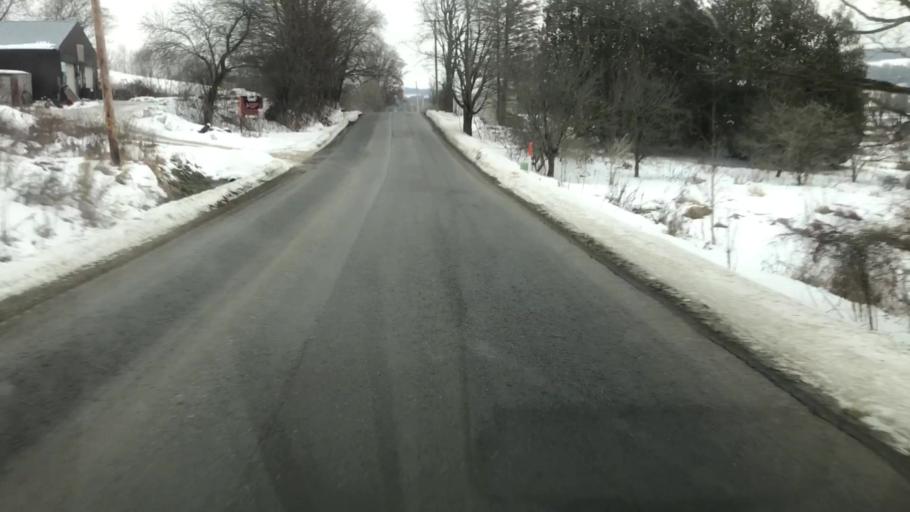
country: US
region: New York
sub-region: Cortland County
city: Cortland West
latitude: 42.6630
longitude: -76.2773
